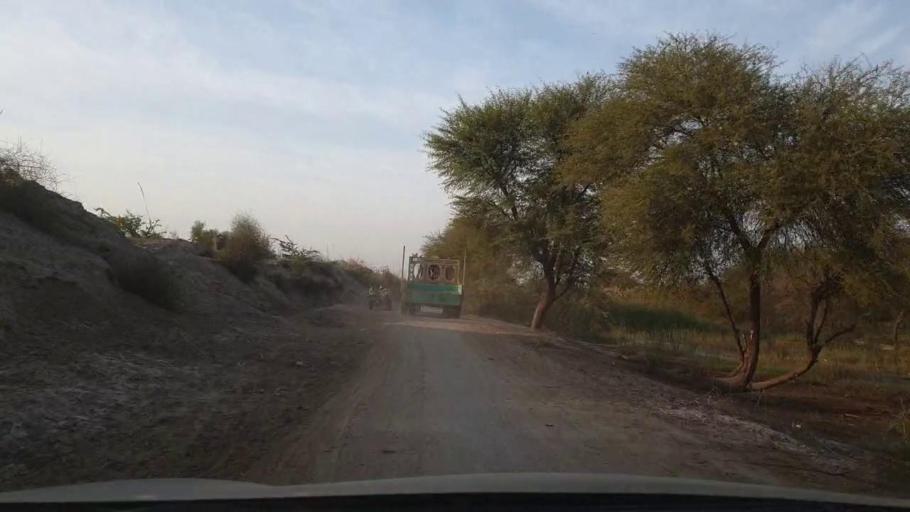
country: PK
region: Sindh
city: Tando Adam
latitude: 25.7057
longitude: 68.7364
